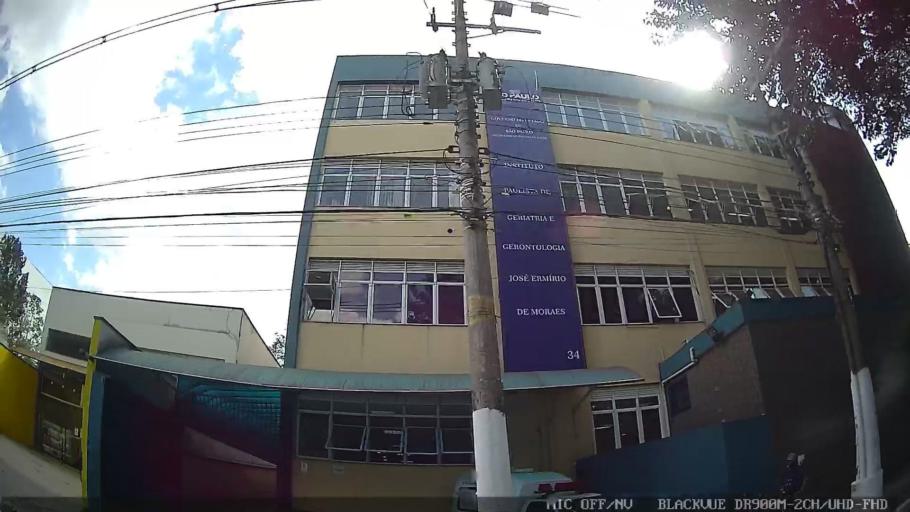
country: BR
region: Sao Paulo
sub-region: Ferraz De Vasconcelos
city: Ferraz de Vasconcelos
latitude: -23.4917
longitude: -46.4460
